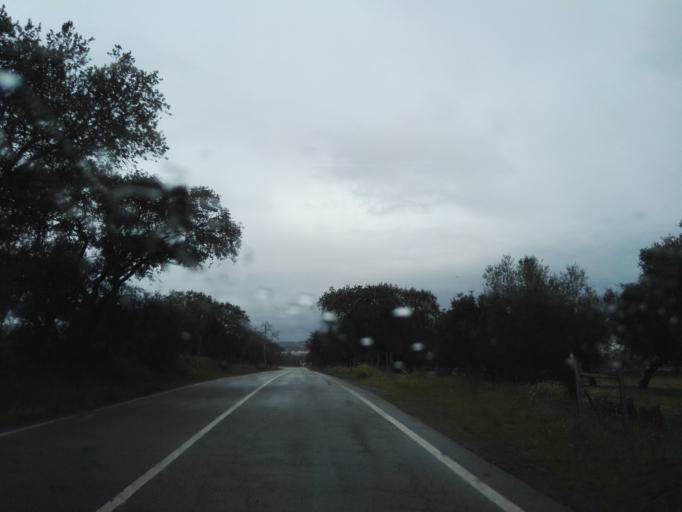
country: PT
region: Portalegre
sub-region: Arronches
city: Arronches
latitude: 39.1103
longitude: -7.2815
